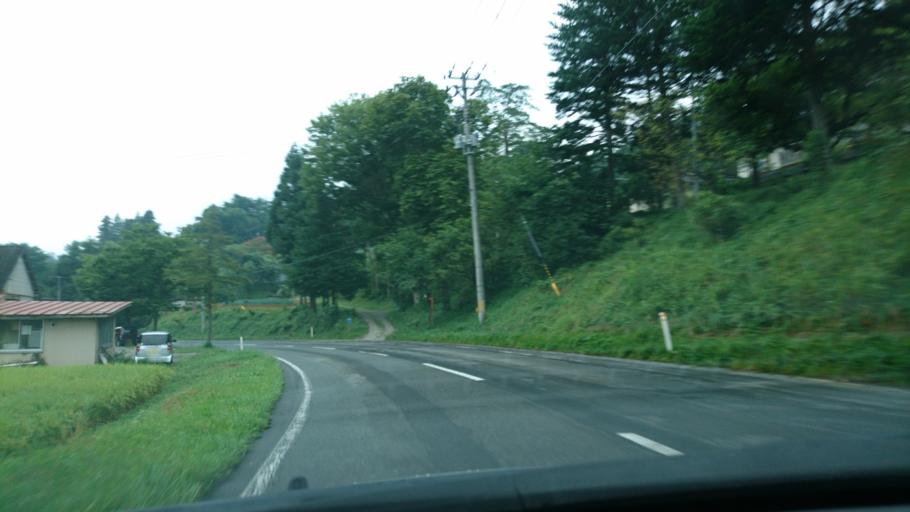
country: JP
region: Iwate
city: Ichinoseki
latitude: 39.0170
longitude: 141.2510
